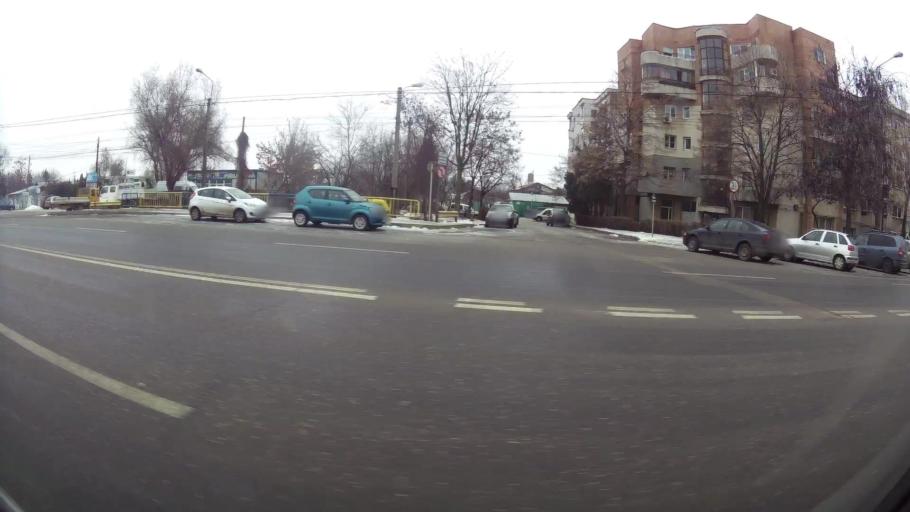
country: RO
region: Prahova
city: Ploiesti
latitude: 44.9393
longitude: 26.0505
